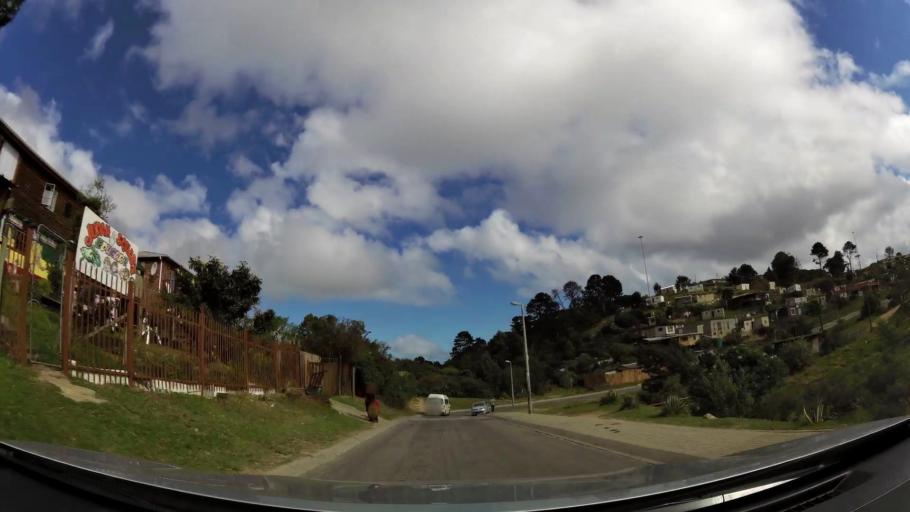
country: ZA
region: Western Cape
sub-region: Eden District Municipality
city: Knysna
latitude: -34.0343
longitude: 23.1021
